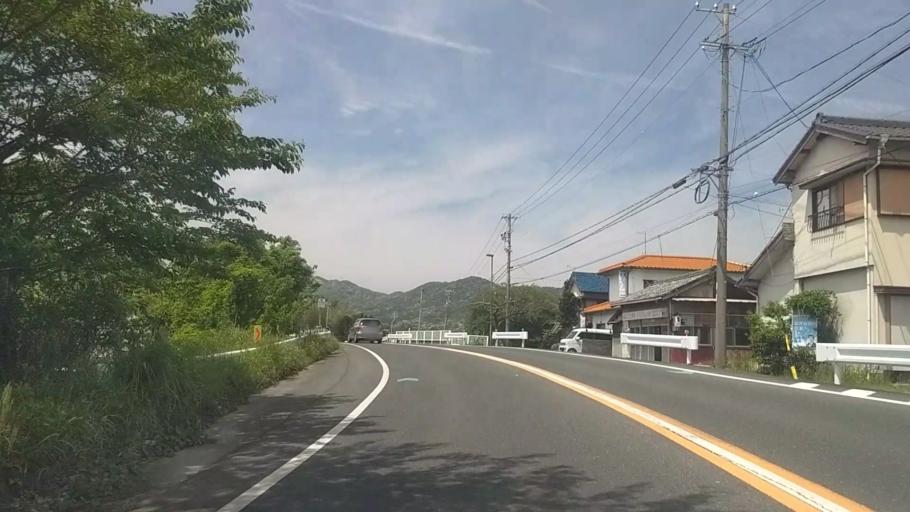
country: JP
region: Shizuoka
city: Kosai-shi
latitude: 34.7496
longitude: 137.5119
